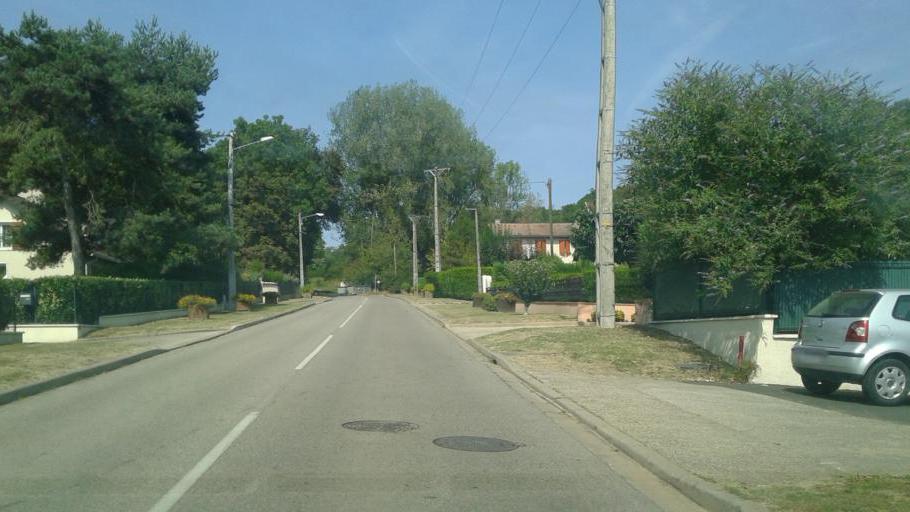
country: FR
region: Rhone-Alpes
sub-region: Departement de l'Ain
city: La Boisse
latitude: 45.8461
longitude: 5.0317
